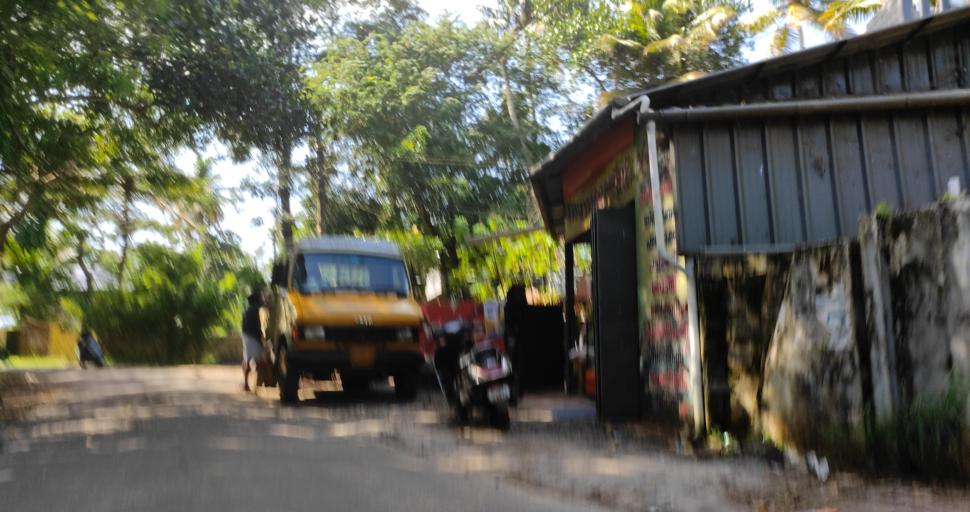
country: IN
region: Kerala
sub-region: Alappuzha
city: Shertallai
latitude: 9.6267
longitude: 76.3380
